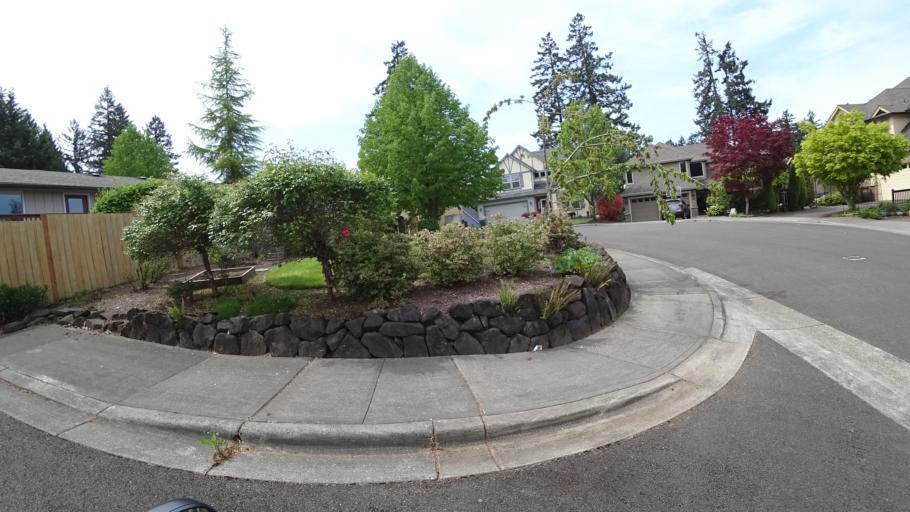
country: US
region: Oregon
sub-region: Washington County
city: Aloha
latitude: 45.4639
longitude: -122.8589
